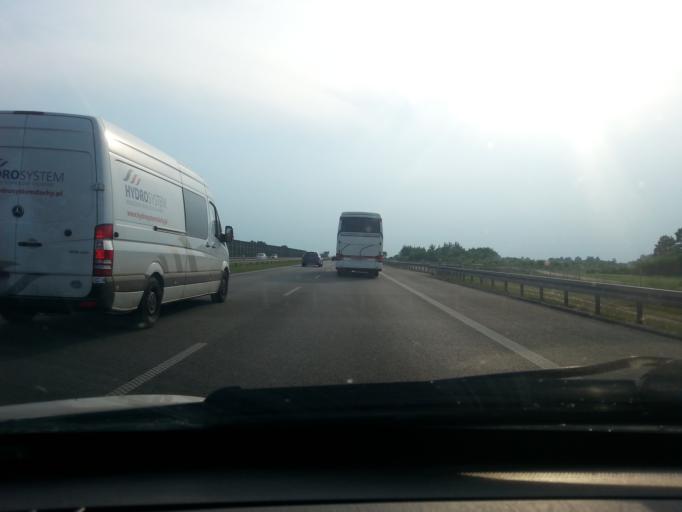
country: PL
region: Masovian Voivodeship
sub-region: Powiat grodziski
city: Milanowek
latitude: 52.1490
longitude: 20.6417
